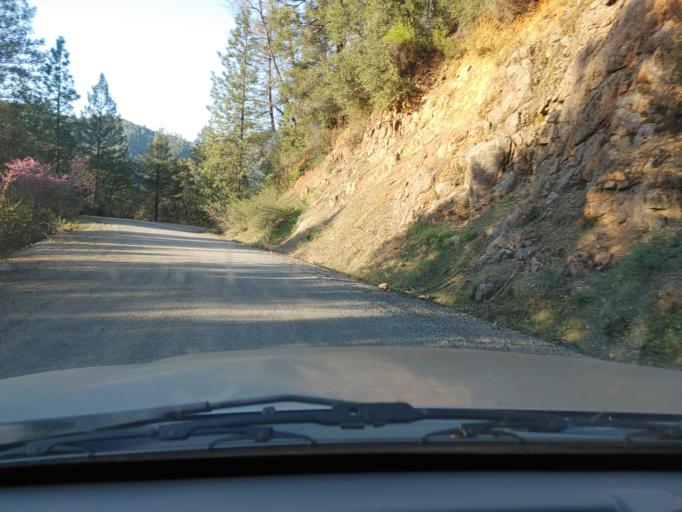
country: US
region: California
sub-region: Shasta County
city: Bella Vista
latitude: 40.8379
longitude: -122.0170
